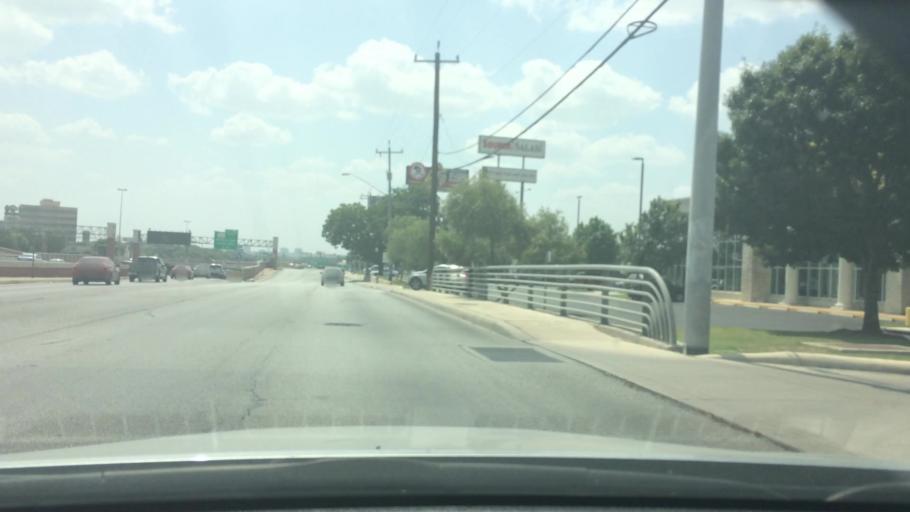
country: US
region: Texas
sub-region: Bexar County
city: Castle Hills
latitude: 29.5209
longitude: -98.5034
